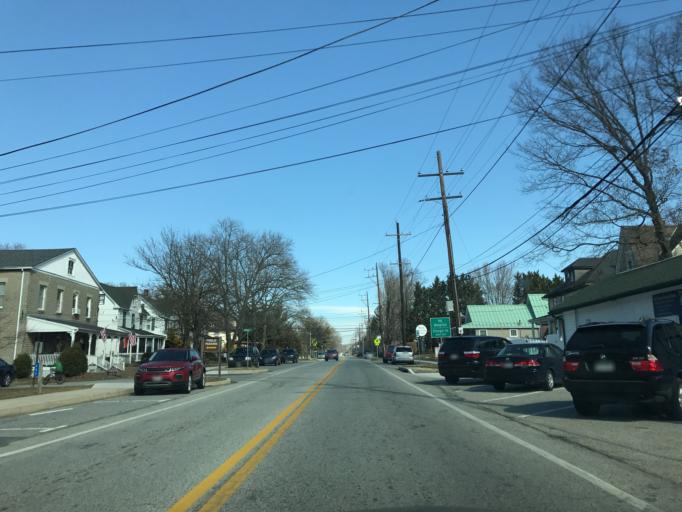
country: US
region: Maryland
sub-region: Cecil County
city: Perryville
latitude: 39.5604
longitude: -76.0714
